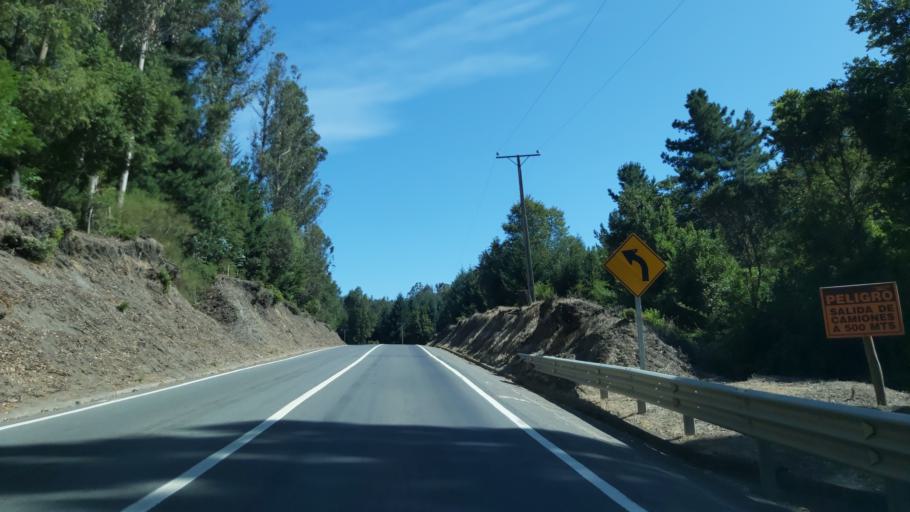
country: CL
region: Biobio
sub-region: Provincia de Concepcion
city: Lota
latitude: -37.1223
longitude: -72.9858
